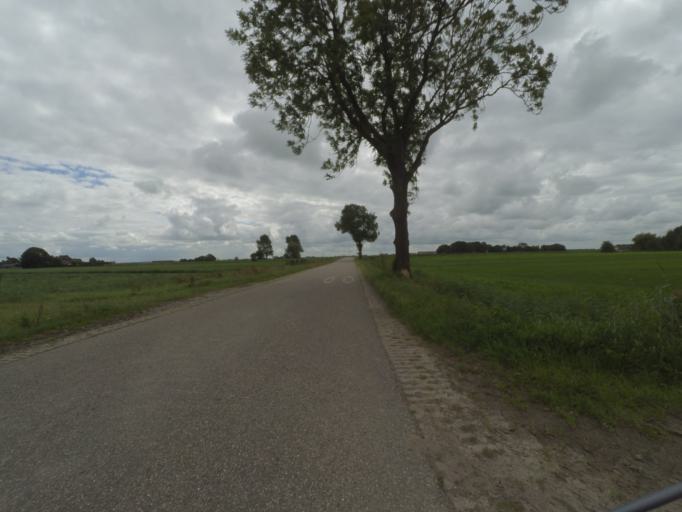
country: NL
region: Friesland
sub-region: Gemeente Dongeradeel
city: Anjum
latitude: 53.3216
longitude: 6.1013
